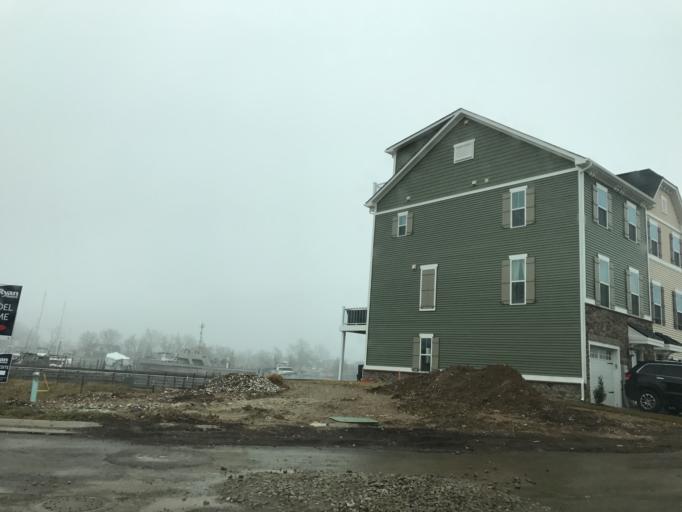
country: US
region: Maryland
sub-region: Baltimore County
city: Dundalk
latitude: 39.2554
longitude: -76.4958
